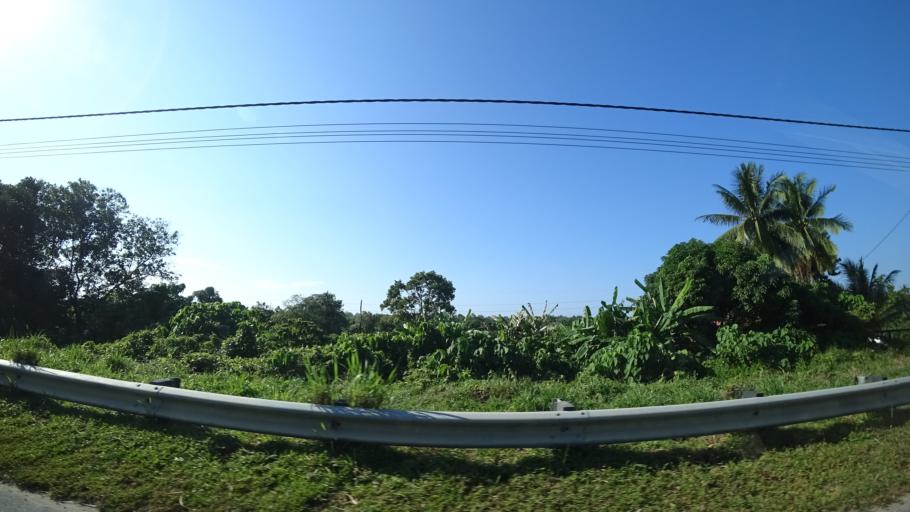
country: BN
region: Tutong
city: Tutong
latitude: 4.6831
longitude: 114.5027
